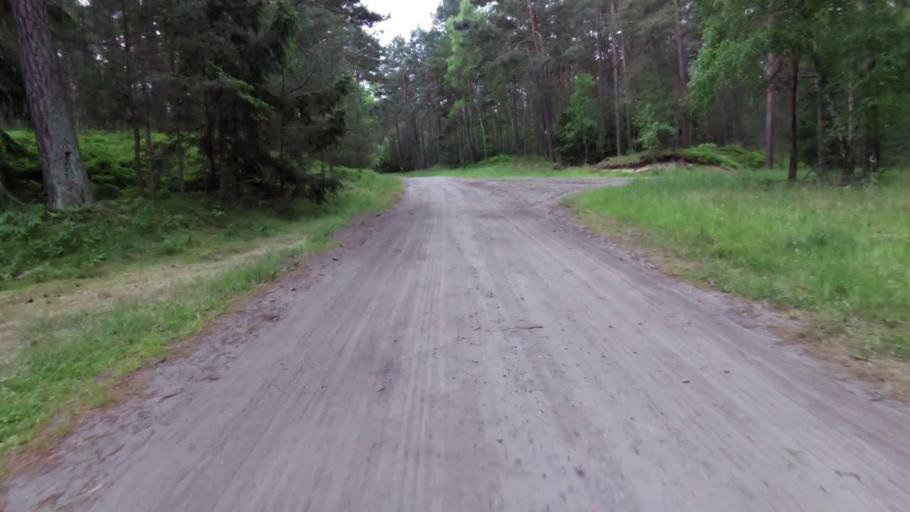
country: PL
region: West Pomeranian Voivodeship
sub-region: Swinoujscie
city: Swinoujscie
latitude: 53.9011
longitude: 14.3327
